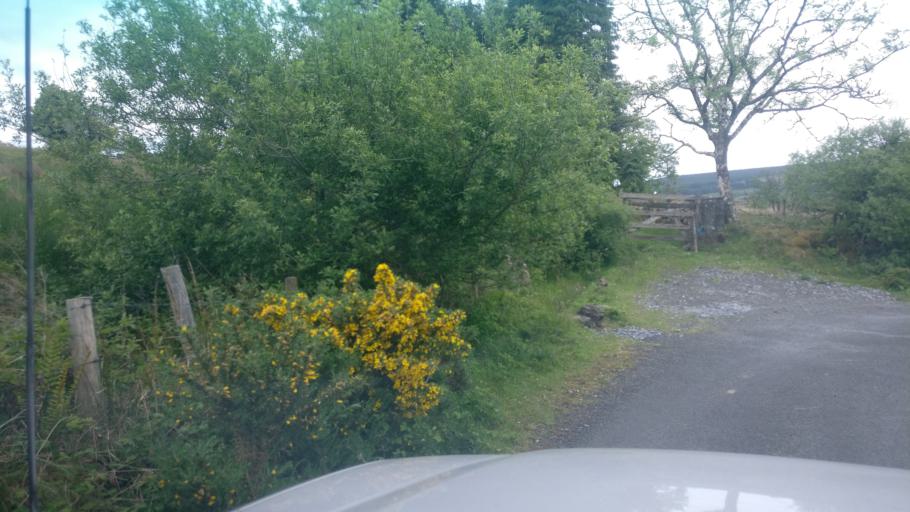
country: IE
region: Connaught
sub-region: County Galway
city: Loughrea
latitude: 53.1169
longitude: -8.6354
